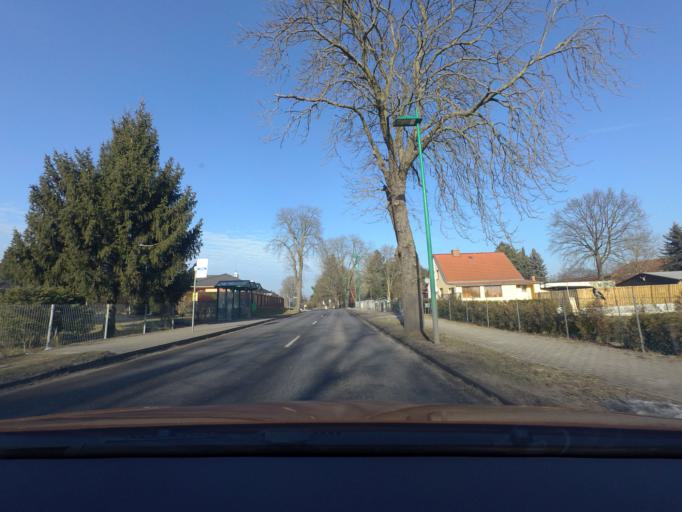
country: DE
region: Berlin
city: Blankenfelde
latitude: 52.6846
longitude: 13.3727
